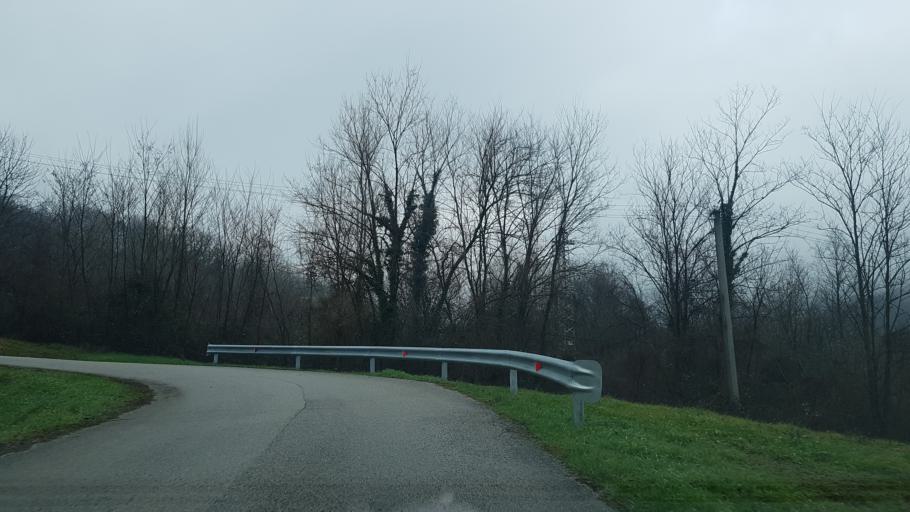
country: IT
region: Friuli Venezia Giulia
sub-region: Provincia di Udine
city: Prepotto
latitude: 46.0758
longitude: 13.4781
